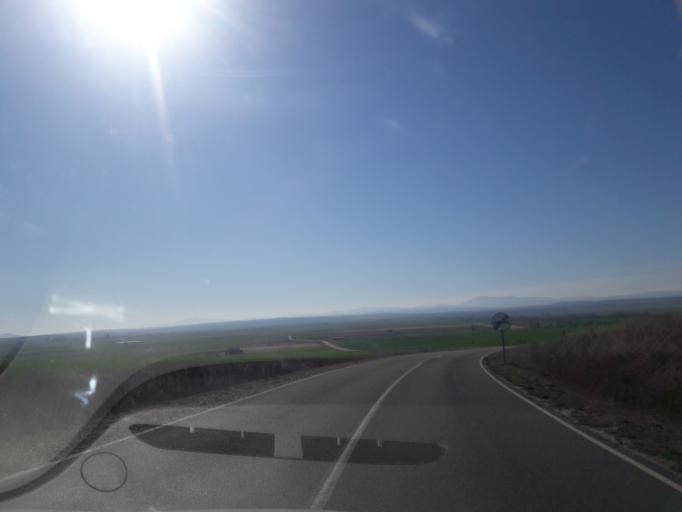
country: ES
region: Castille and Leon
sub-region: Provincia de Salamanca
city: Macotera
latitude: 40.8213
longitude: -5.2653
